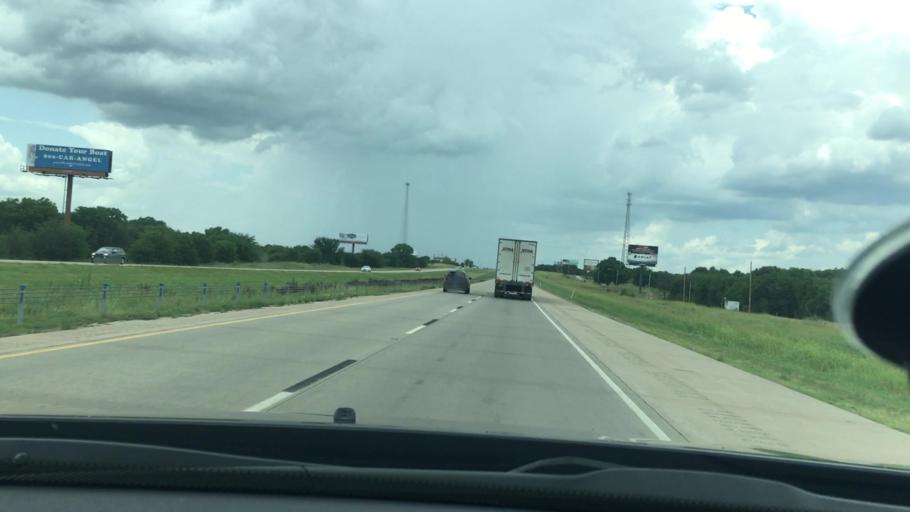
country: US
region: Oklahoma
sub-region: Carter County
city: Ardmore
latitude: 34.2663
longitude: -97.1634
